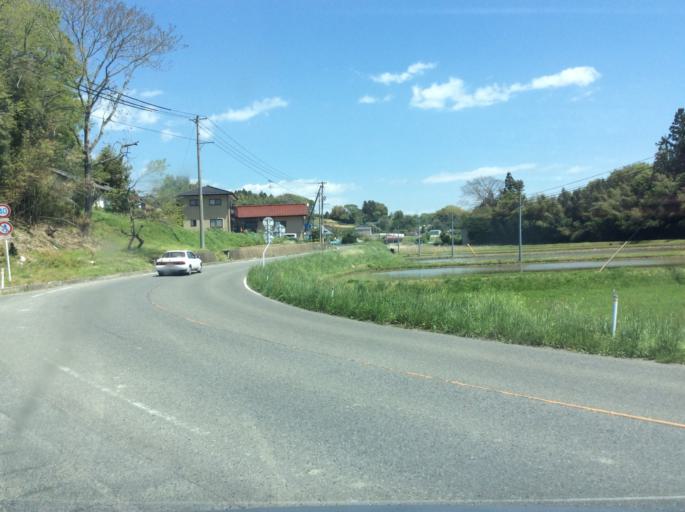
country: JP
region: Fukushima
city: Miharu
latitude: 37.4486
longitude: 140.5131
